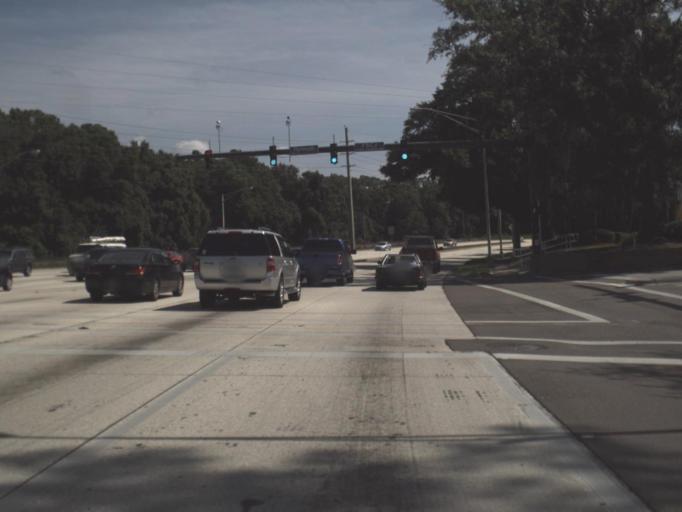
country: US
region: Florida
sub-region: Duval County
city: Jacksonville
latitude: 30.3024
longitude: -81.7198
